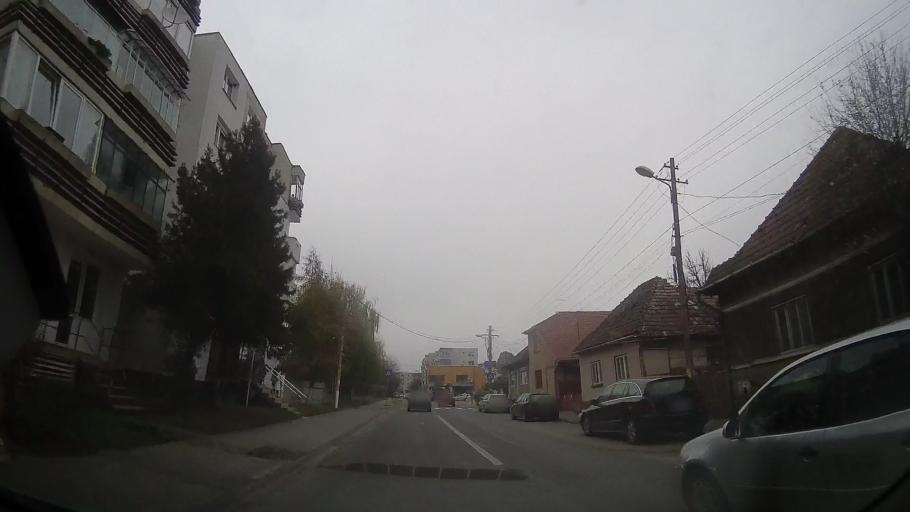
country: RO
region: Mures
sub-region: Comuna Santana de Mures
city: Santana de Mures
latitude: 46.5660
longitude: 24.5480
